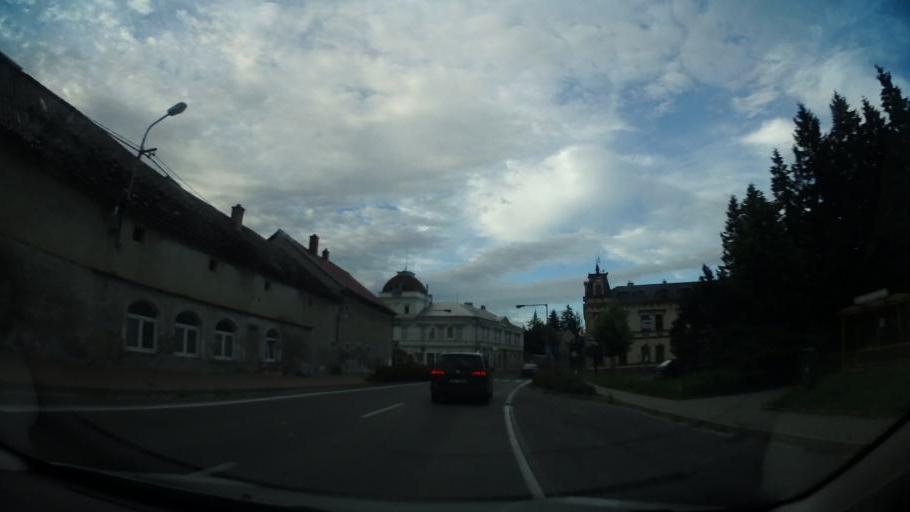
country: CZ
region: Olomoucky
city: Cervenka
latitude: 49.7499
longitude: 17.0918
